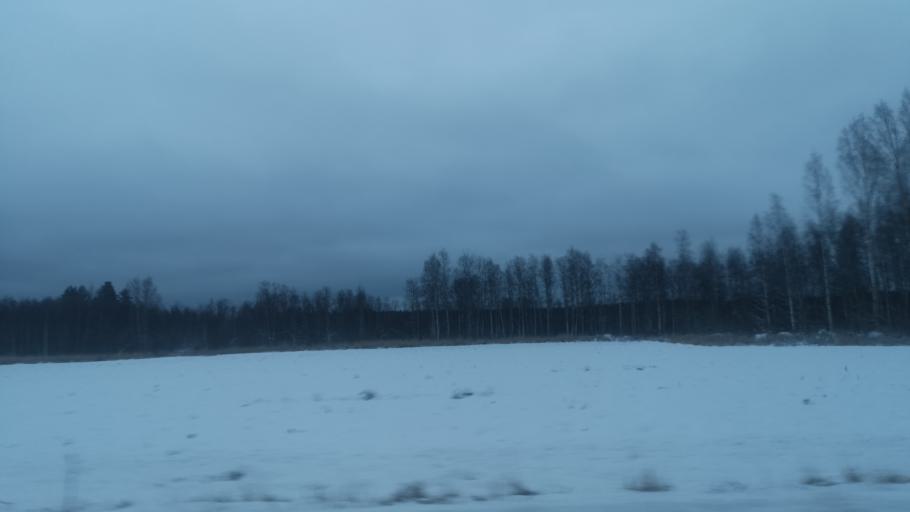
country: FI
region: Southern Savonia
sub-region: Savonlinna
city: Enonkoski
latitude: 62.0829
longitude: 28.6967
